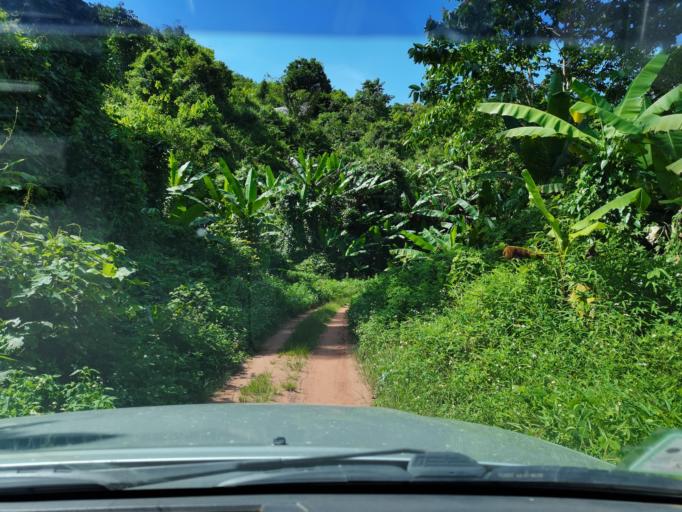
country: LA
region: Loungnamtha
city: Muang Nale
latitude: 20.5442
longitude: 101.0627
